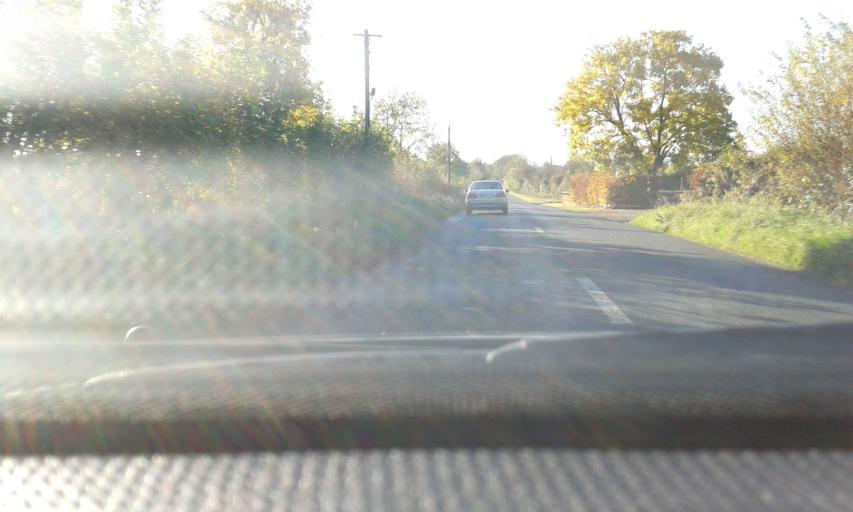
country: IE
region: Leinster
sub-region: Kildare
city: Rathangan
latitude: 53.1989
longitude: -7.0046
